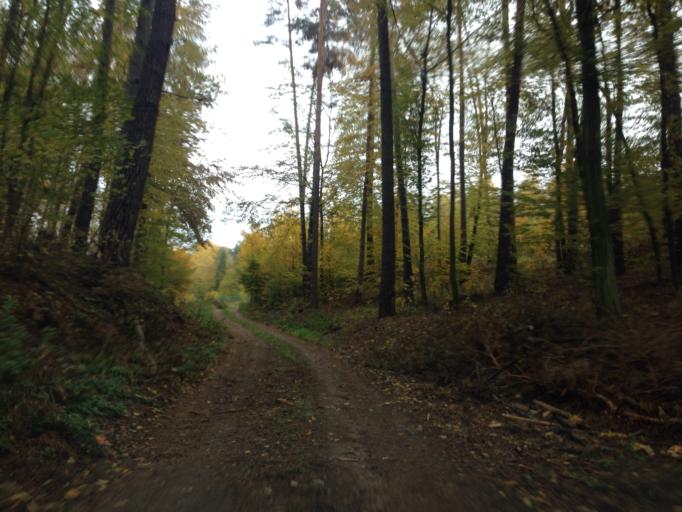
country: PL
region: Kujawsko-Pomorskie
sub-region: Powiat brodnicki
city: Gorzno
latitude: 53.2568
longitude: 19.6899
